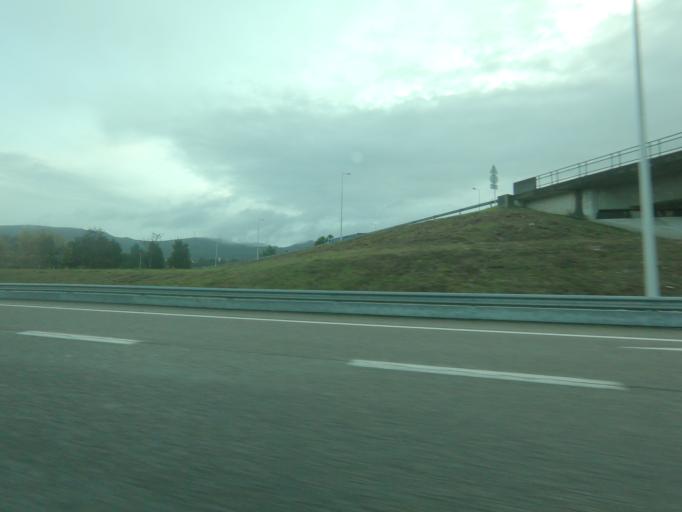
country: PT
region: Viana do Castelo
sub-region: Valenca
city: Valenza
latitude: 41.9875
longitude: -8.6462
